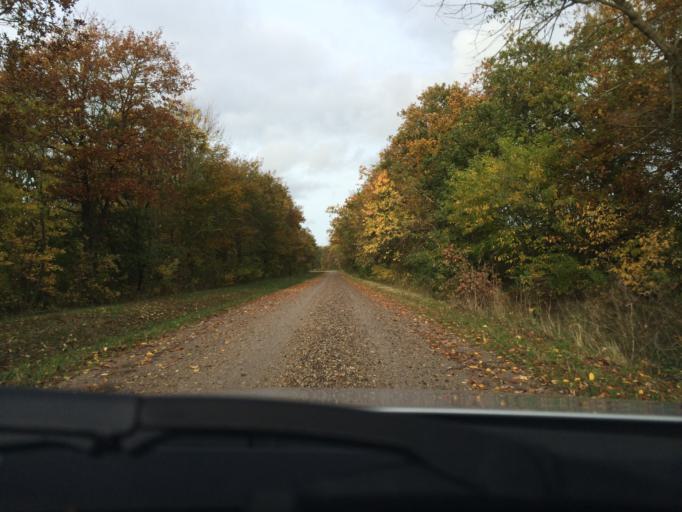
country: DK
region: Central Jutland
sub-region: Holstebro Kommune
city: Ulfborg
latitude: 56.2892
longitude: 8.3843
